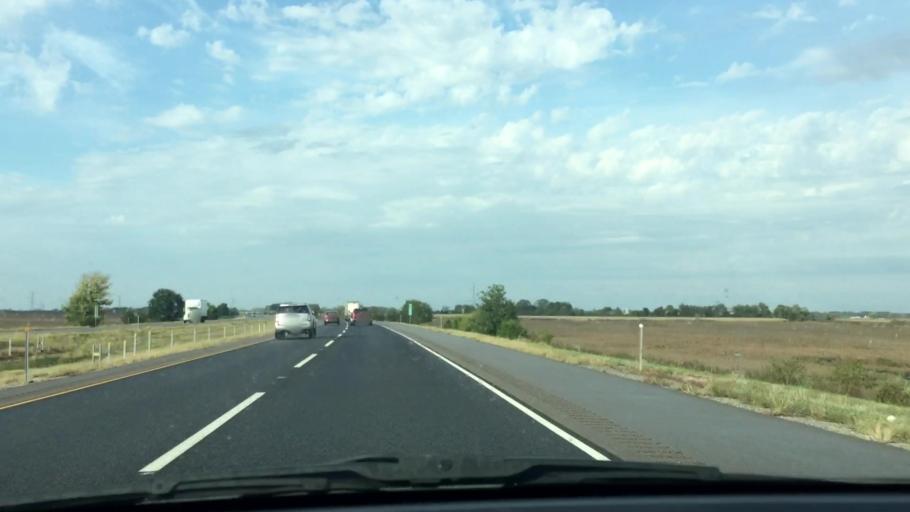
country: US
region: Illinois
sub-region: Lee County
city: Dixon
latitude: 41.7788
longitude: -89.5646
